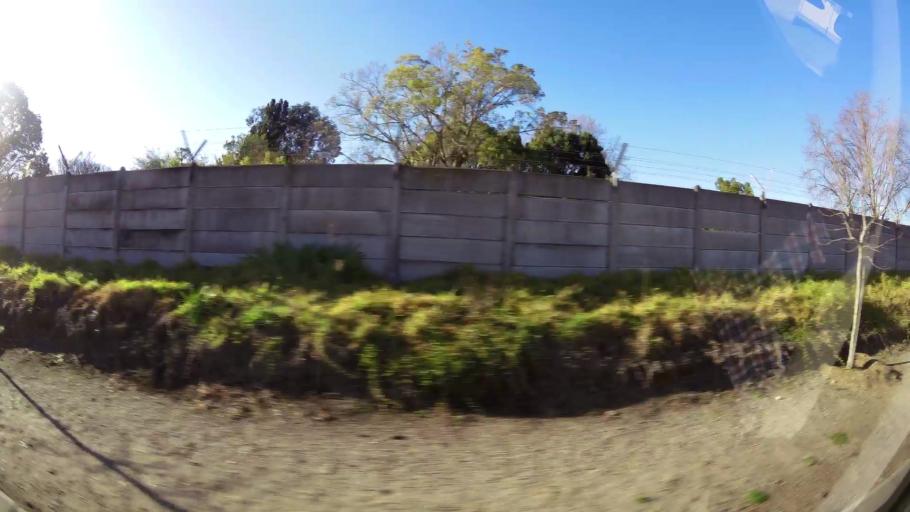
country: ZA
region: Western Cape
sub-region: Eden District Municipality
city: George
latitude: -33.9567
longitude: 22.4457
